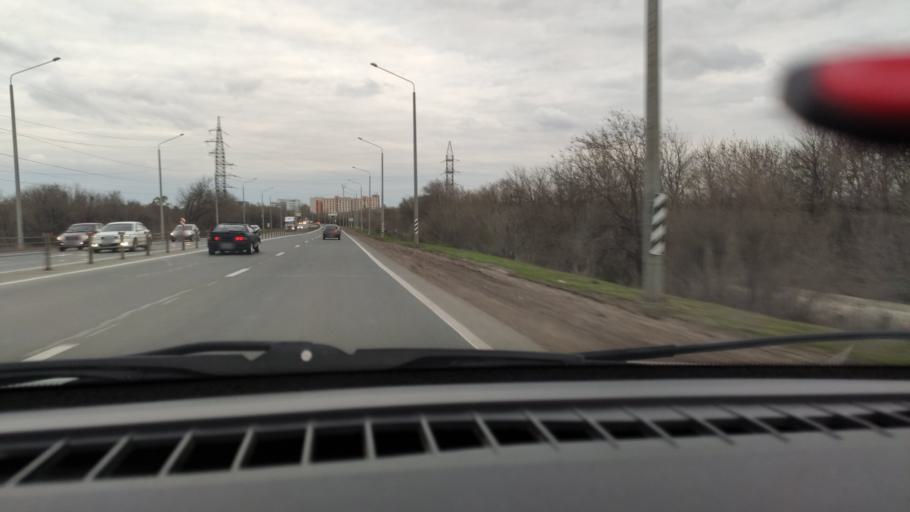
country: RU
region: Orenburg
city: Prigorodnyy
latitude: 51.7882
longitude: 55.1870
